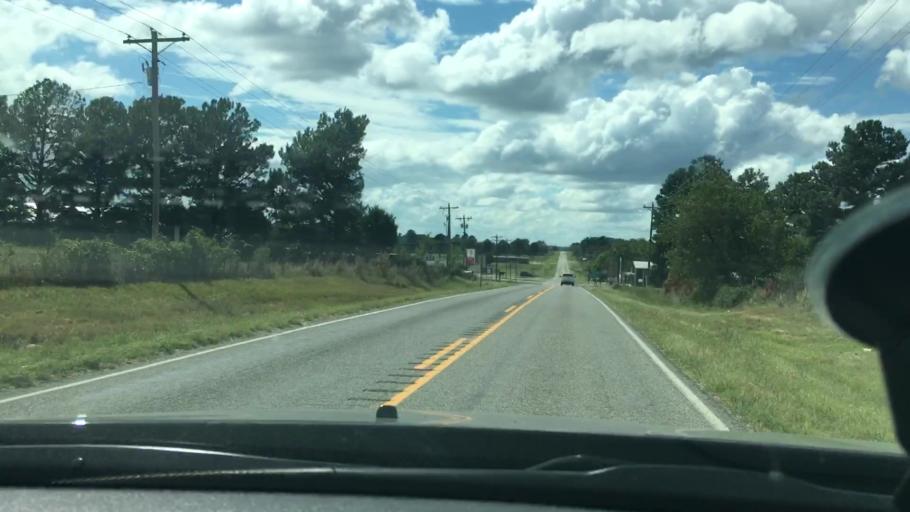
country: US
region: Oklahoma
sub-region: Sequoyah County
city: Vian
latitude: 35.6097
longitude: -94.9731
